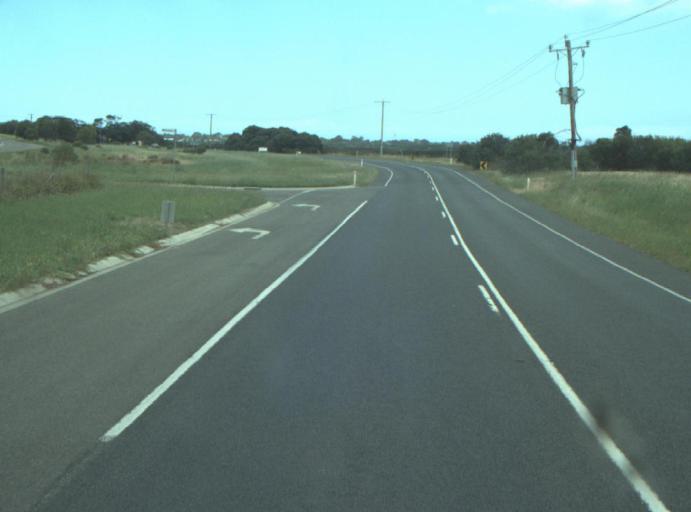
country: AU
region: Victoria
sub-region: Greater Geelong
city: Leopold
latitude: -38.2503
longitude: 144.5039
